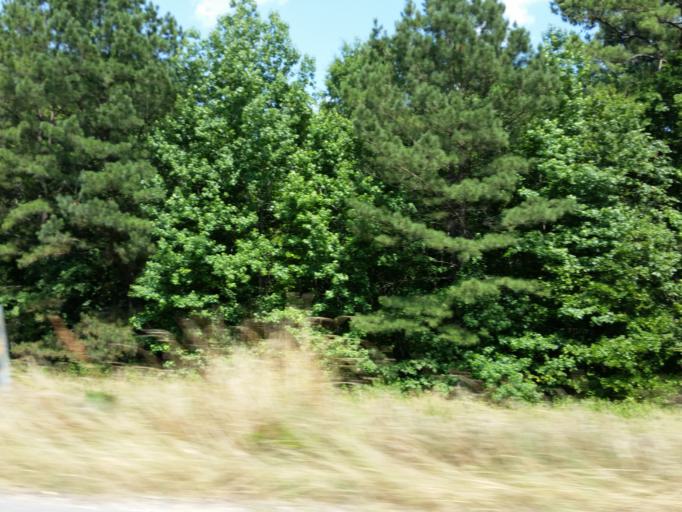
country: US
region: Alabama
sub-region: Marengo County
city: Demopolis
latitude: 32.5534
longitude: -87.8343
